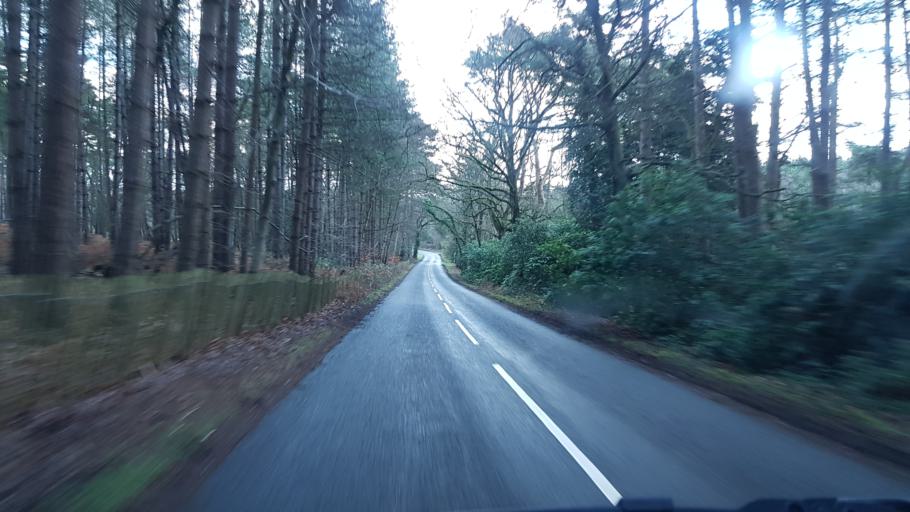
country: GB
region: England
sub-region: Surrey
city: Elstead
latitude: 51.2032
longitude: -0.7096
